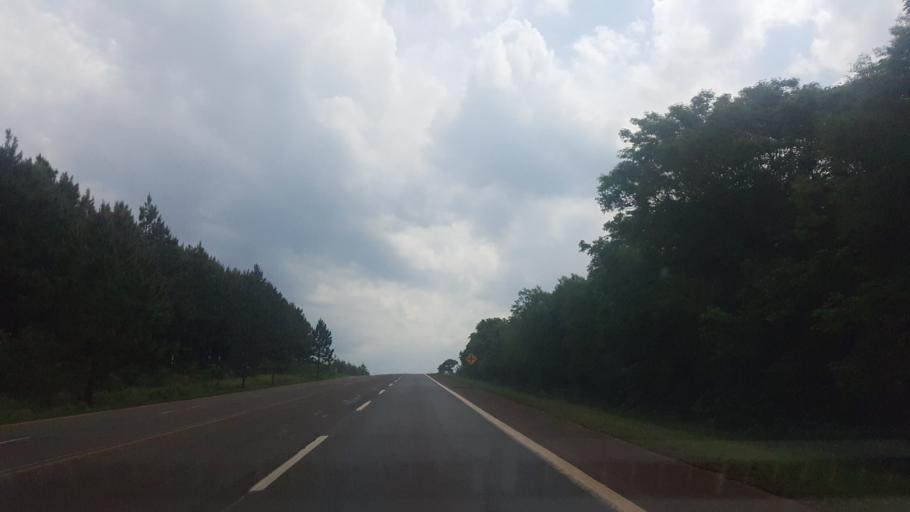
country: AR
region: Misiones
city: Santo Pipo
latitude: -27.1052
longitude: -55.3242
